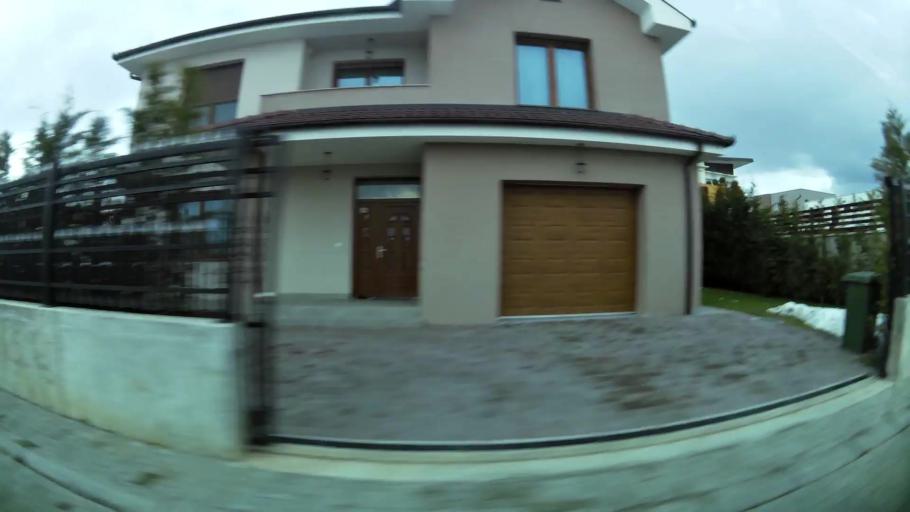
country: XK
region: Pristina
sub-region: Komuna e Prishtines
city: Pristina
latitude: 42.6188
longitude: 21.1661
